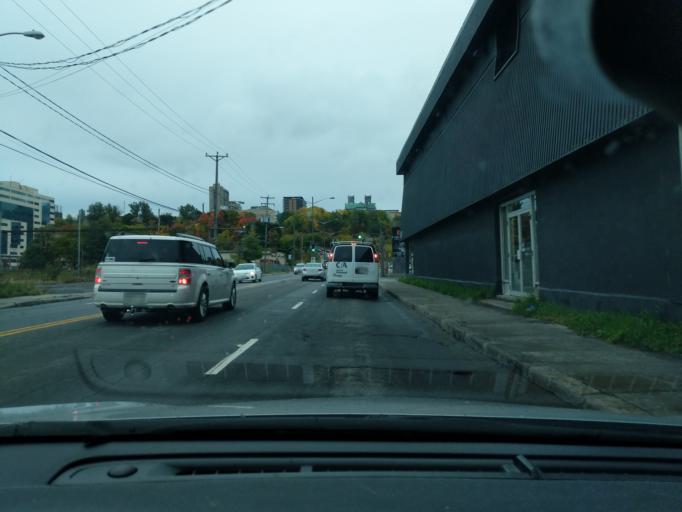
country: CA
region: Quebec
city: Quebec
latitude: 46.8001
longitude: -71.2594
